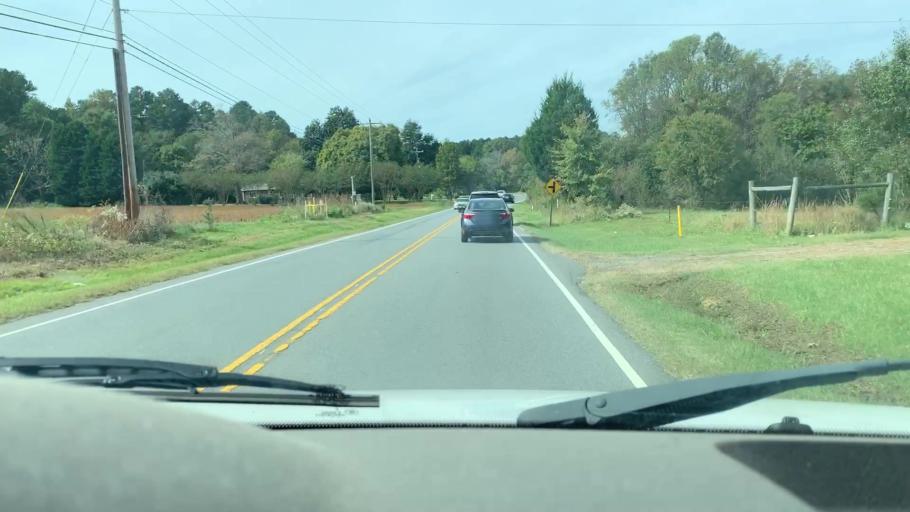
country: US
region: North Carolina
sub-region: Mecklenburg County
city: Huntersville
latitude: 35.4438
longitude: -80.7783
